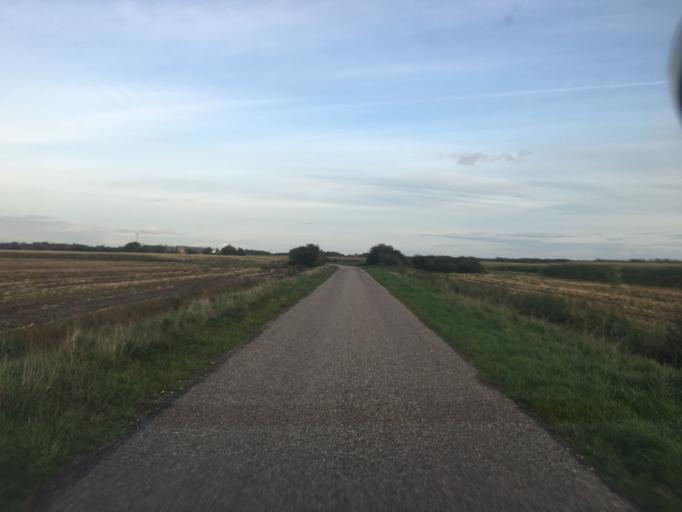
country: DK
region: South Denmark
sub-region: Tonder Kommune
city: Tonder
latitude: 54.9894
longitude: 8.9107
